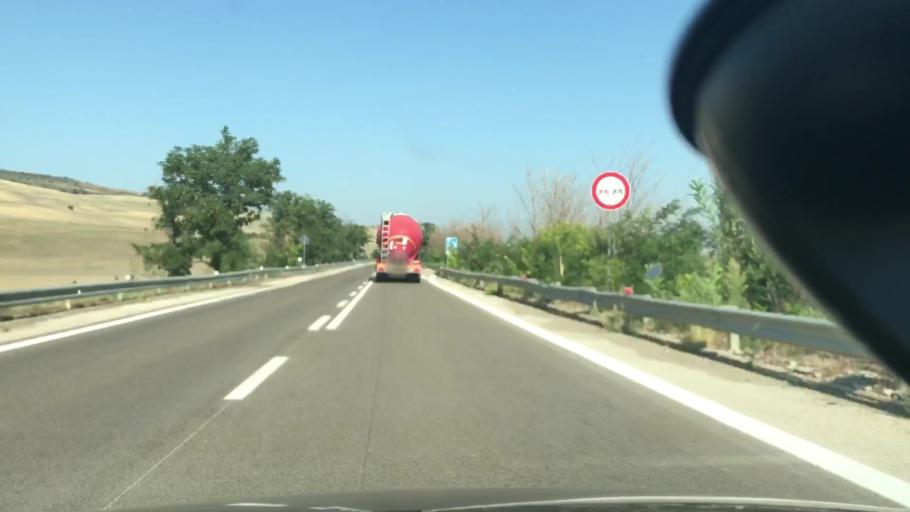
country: IT
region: Basilicate
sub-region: Provincia di Matera
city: Irsina
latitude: 40.7927
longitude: 16.2803
